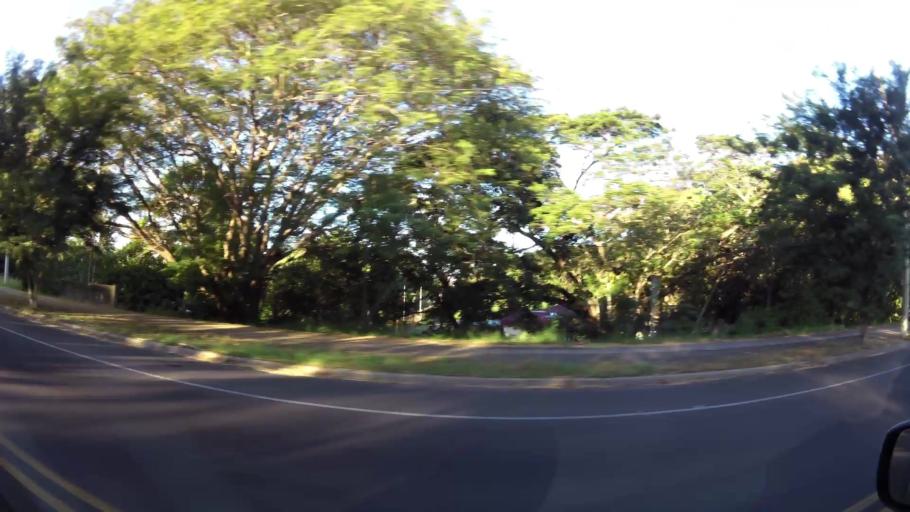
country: CR
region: Puntarenas
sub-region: Canton Central de Puntarenas
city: Chacarita
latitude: 9.9784
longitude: -84.7398
